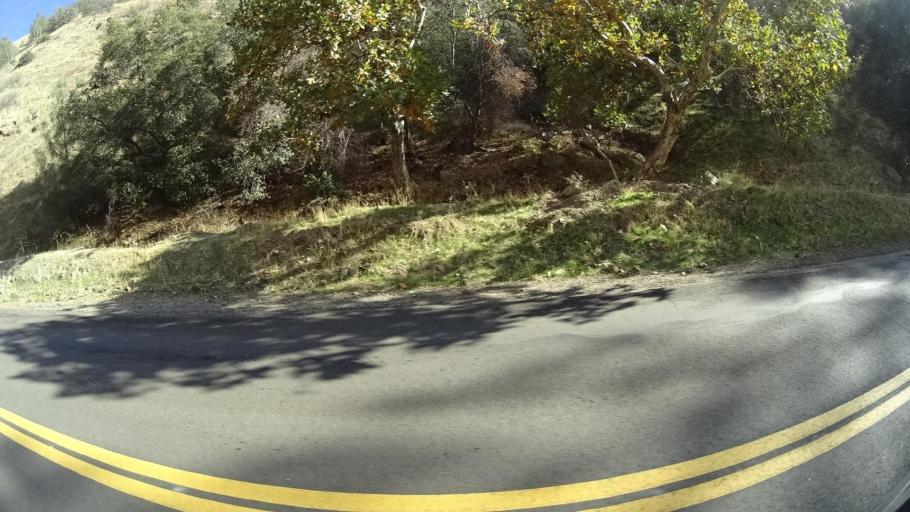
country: US
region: California
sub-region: Kern County
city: Bear Valley Springs
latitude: 35.3346
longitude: -118.5870
